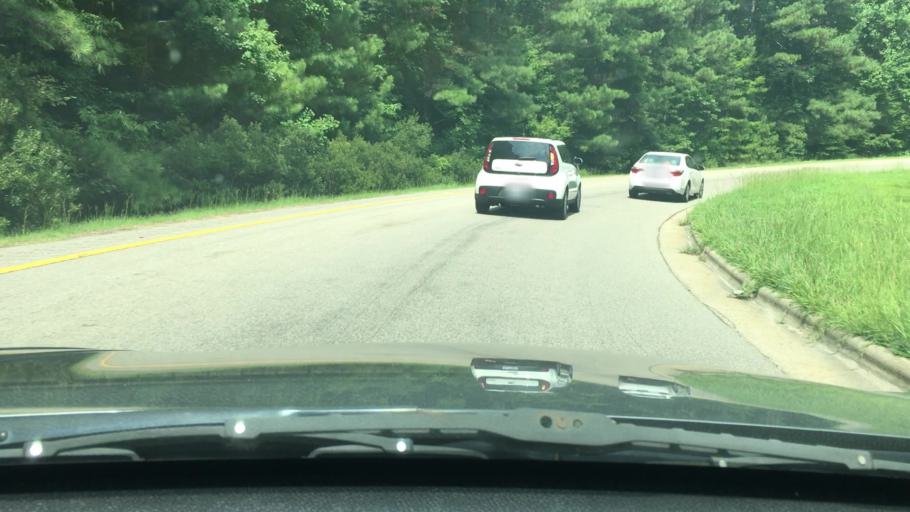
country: US
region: North Carolina
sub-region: Wake County
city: Cary
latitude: 35.8192
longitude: -78.7390
